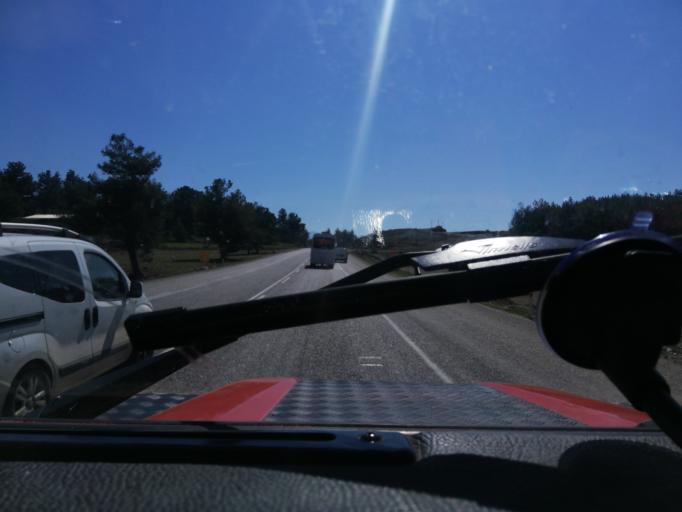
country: TR
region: Mugla
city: Kemer
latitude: 36.6127
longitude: 29.3579
